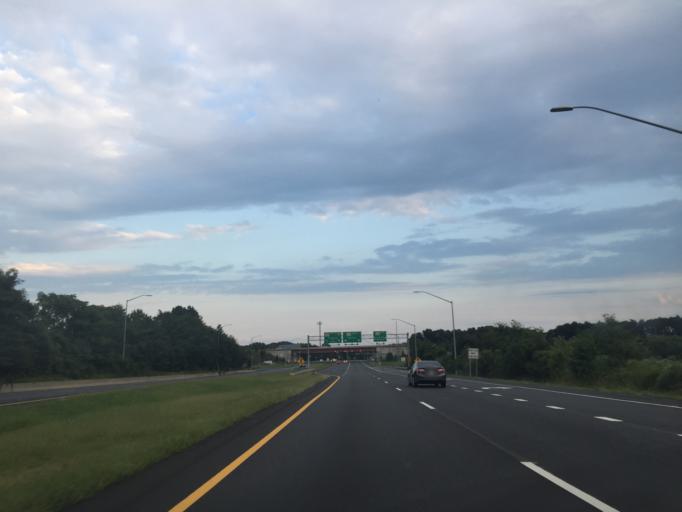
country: US
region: Maryland
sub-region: Anne Arundel County
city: Severn
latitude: 39.1516
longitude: -76.6906
